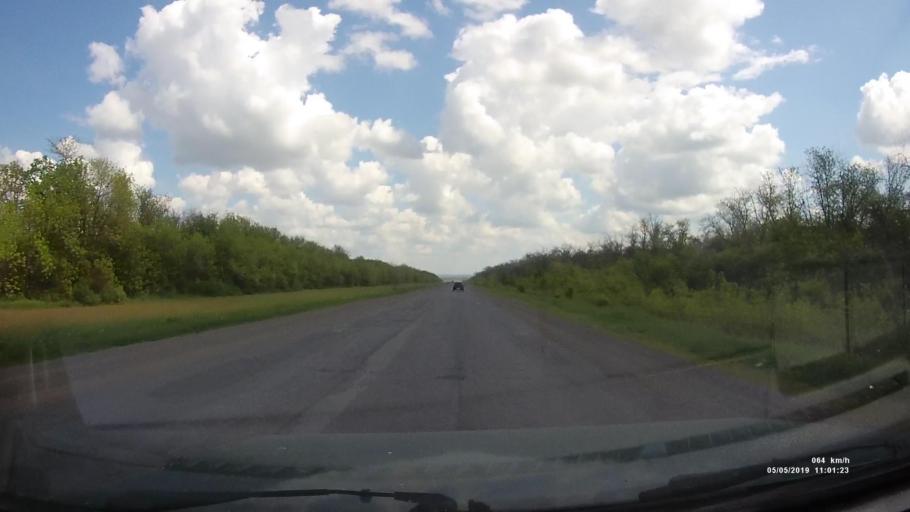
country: RU
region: Rostov
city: Ust'-Donetskiy
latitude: 47.6792
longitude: 40.8986
